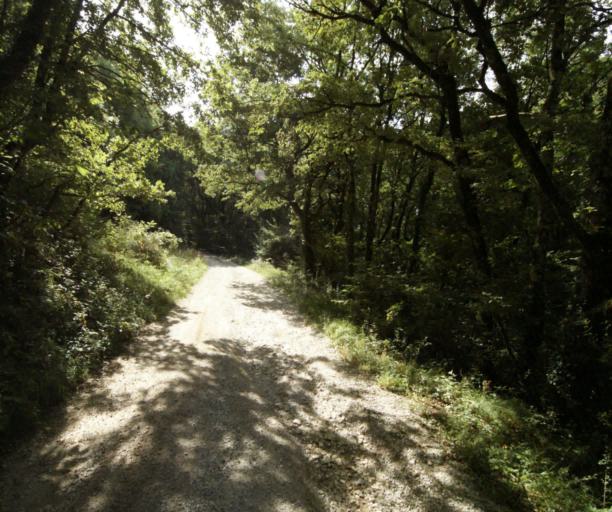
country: FR
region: Midi-Pyrenees
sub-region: Departement du Tarn
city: Dourgne
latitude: 43.4620
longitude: 2.1077
